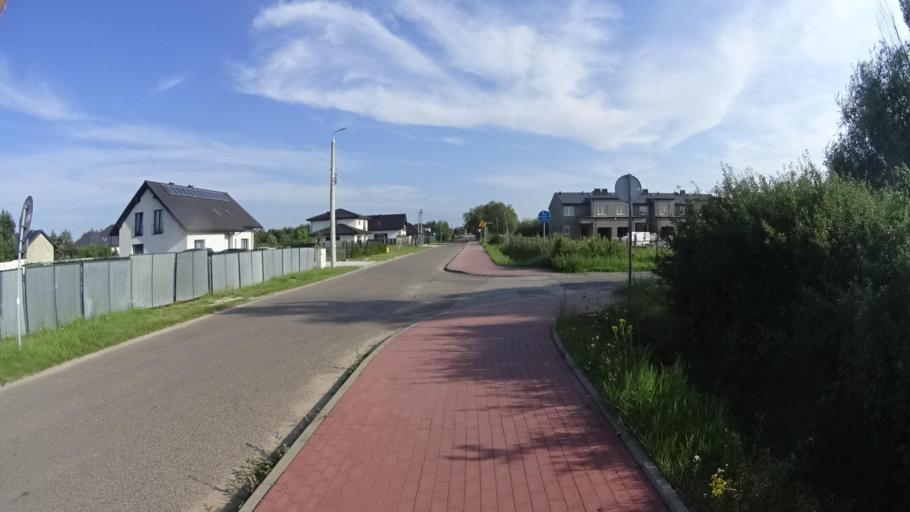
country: PL
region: Masovian Voivodeship
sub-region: Powiat pruszkowski
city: Nadarzyn
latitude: 52.0673
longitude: 20.7876
